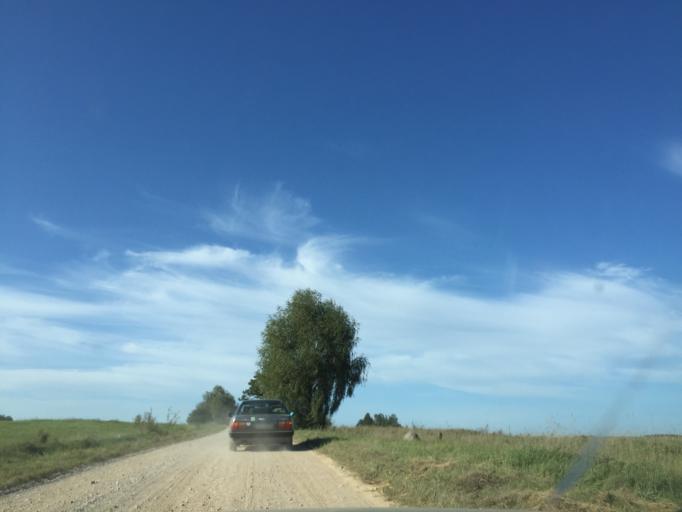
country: LT
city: Zarasai
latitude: 55.7999
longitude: 25.9488
